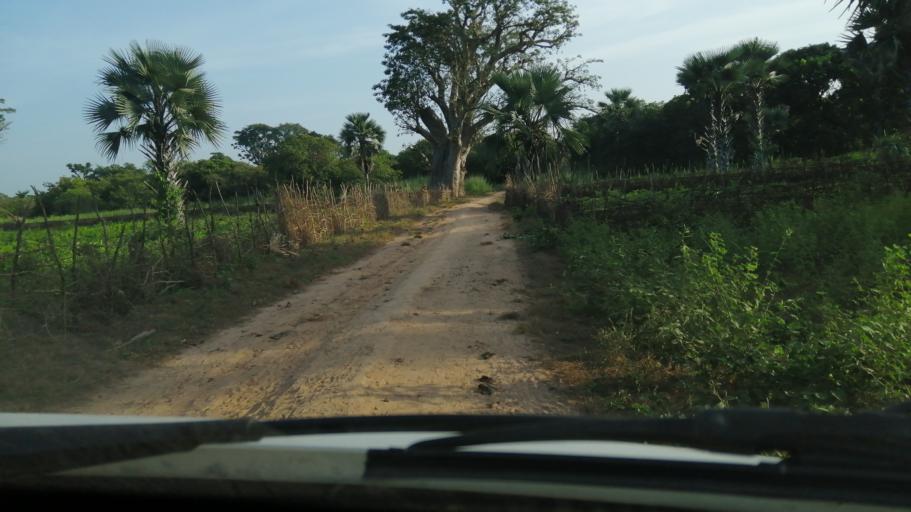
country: GW
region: Oio
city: Mansoa
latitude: 12.0008
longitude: -15.4722
